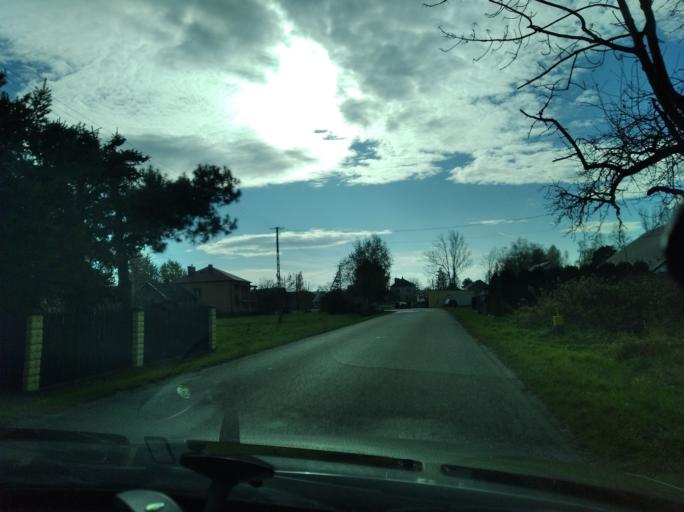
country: PL
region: Subcarpathian Voivodeship
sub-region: Powiat ropczycko-sedziszowski
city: Ostrow
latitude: 50.0945
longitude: 21.5546
